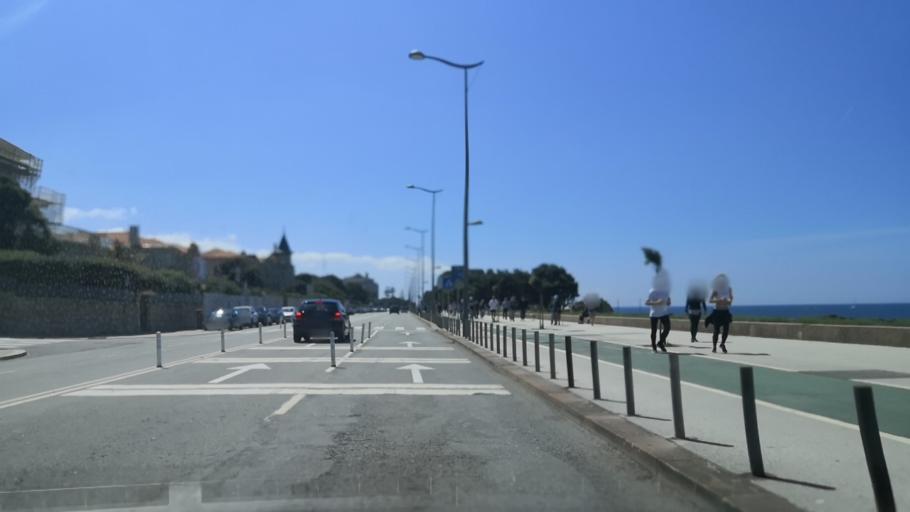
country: PT
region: Porto
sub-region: Matosinhos
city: Matosinhos
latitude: 41.1632
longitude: -8.6859
